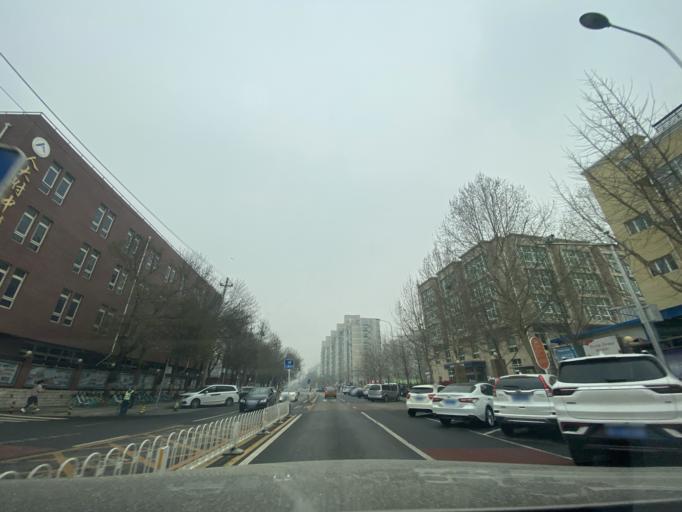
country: CN
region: Beijing
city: Sijiqing
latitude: 39.9650
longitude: 116.2726
